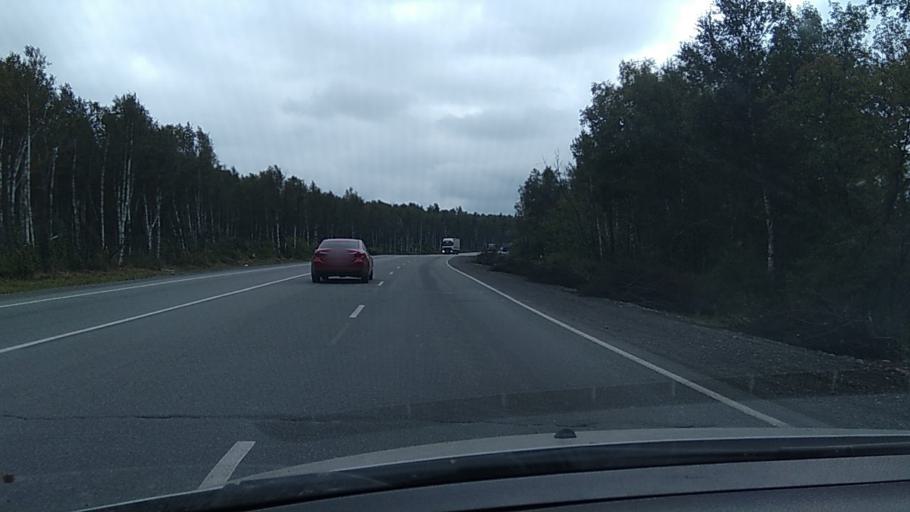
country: RU
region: Chelyabinsk
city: Zlatoust
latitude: 55.0489
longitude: 59.7223
